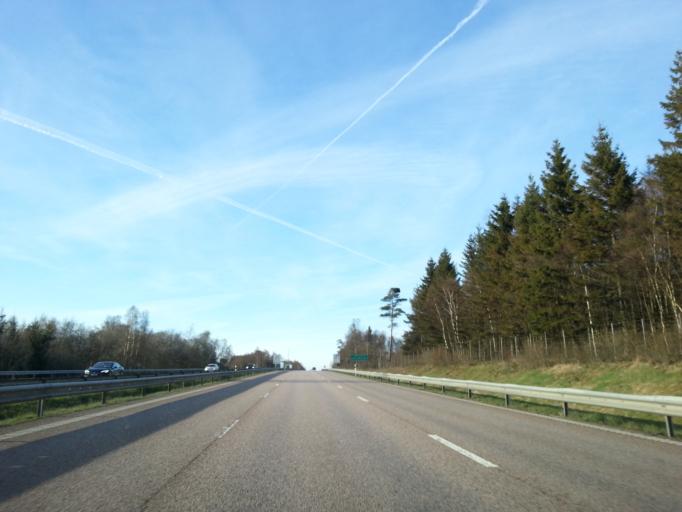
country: SE
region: Skane
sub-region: Bastads Kommun
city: Bastad
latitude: 56.3832
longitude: 12.9362
